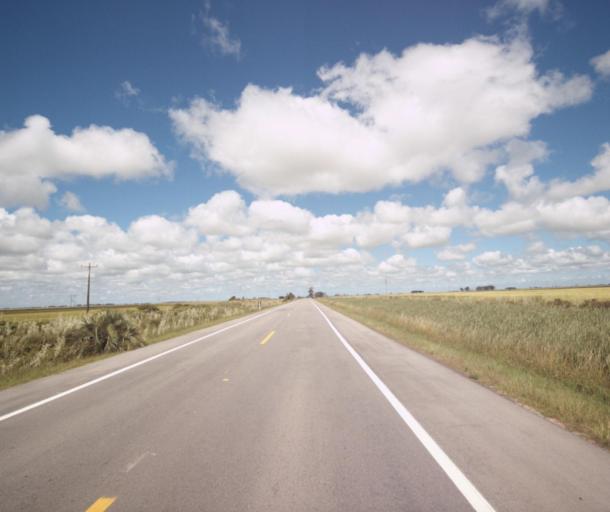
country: BR
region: Rio Grande do Sul
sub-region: Rio Grande
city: Rio Grande
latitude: -32.1513
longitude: -52.3920
